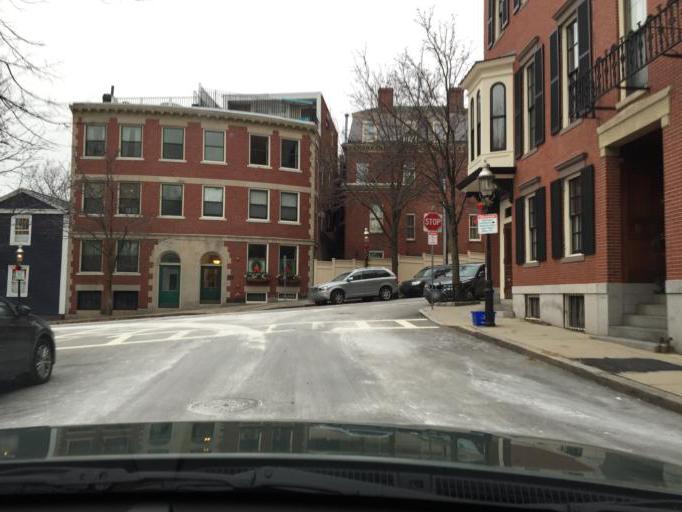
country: US
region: Massachusetts
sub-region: Suffolk County
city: Boston
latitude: 42.3747
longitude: -71.0599
